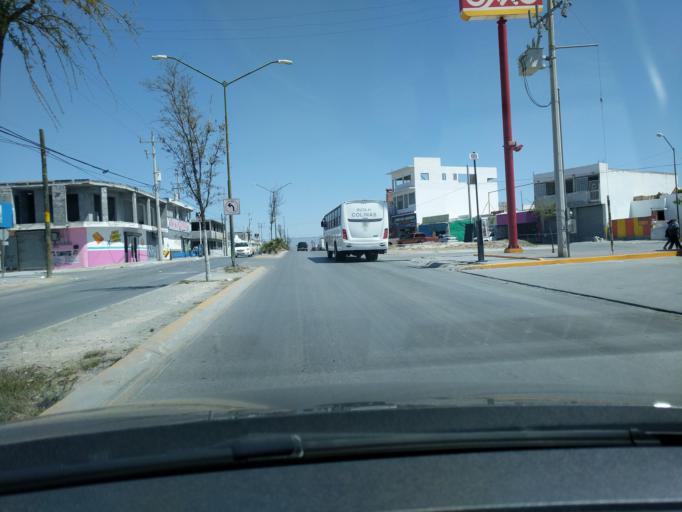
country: MX
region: Nuevo Leon
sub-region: Pesqueria
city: Colinas del Aeropuerto
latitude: 25.8177
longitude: -100.1081
